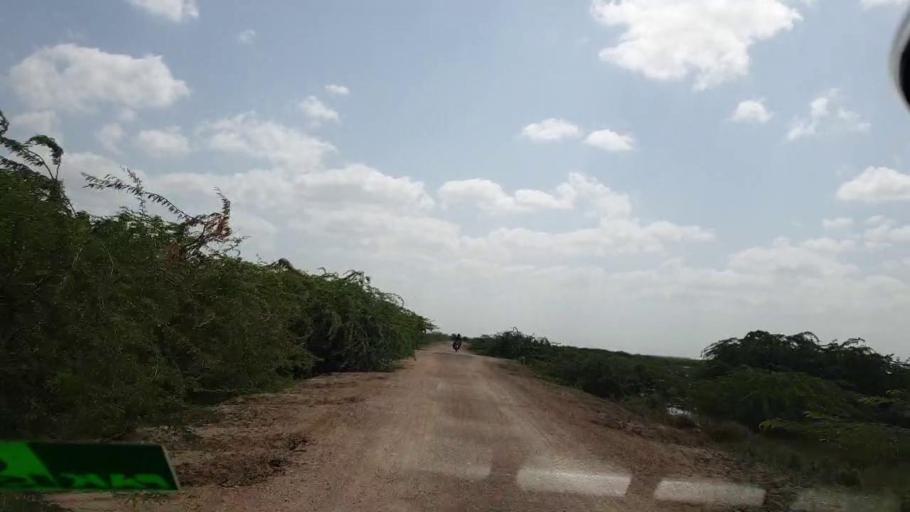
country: PK
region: Sindh
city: Kadhan
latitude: 24.5933
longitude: 69.1832
